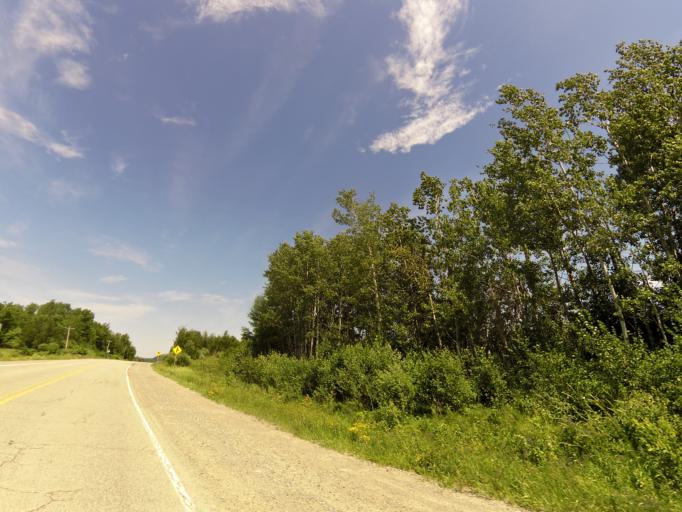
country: CA
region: Quebec
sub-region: Abitibi-Temiscamingue
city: Ville-Marie
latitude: 47.2641
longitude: -79.4113
